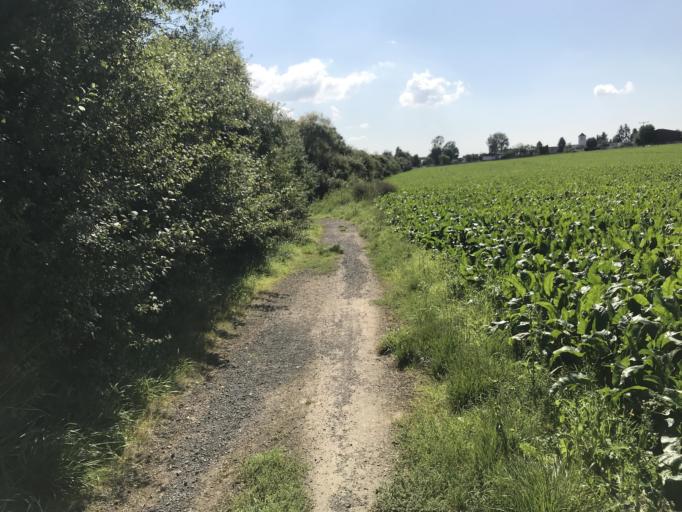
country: DE
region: Hesse
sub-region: Regierungsbezirk Giessen
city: Hungen
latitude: 50.4407
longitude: 8.8901
